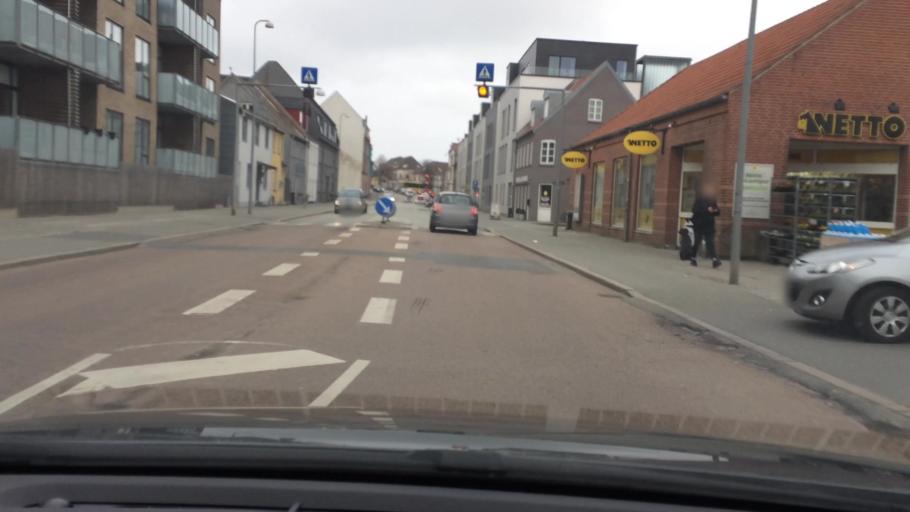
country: DK
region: Central Jutland
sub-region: Horsens Kommune
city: Horsens
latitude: 55.8701
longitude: 9.8411
